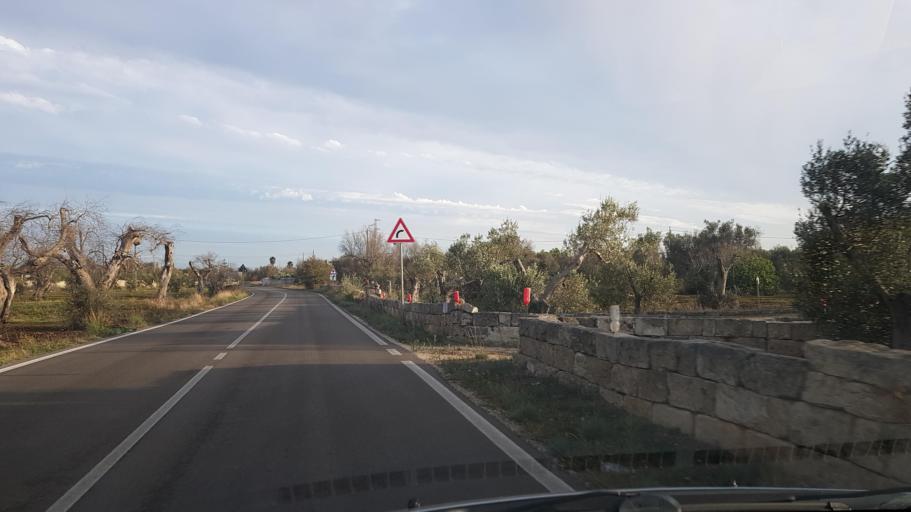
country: IT
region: Apulia
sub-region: Provincia di Lecce
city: Surbo
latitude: 40.4125
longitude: 18.1243
